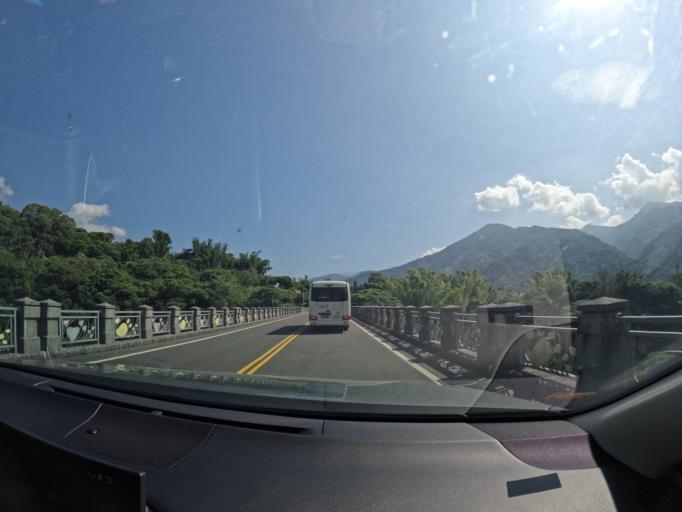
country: TW
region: Taiwan
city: Yujing
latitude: 23.0708
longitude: 120.6700
